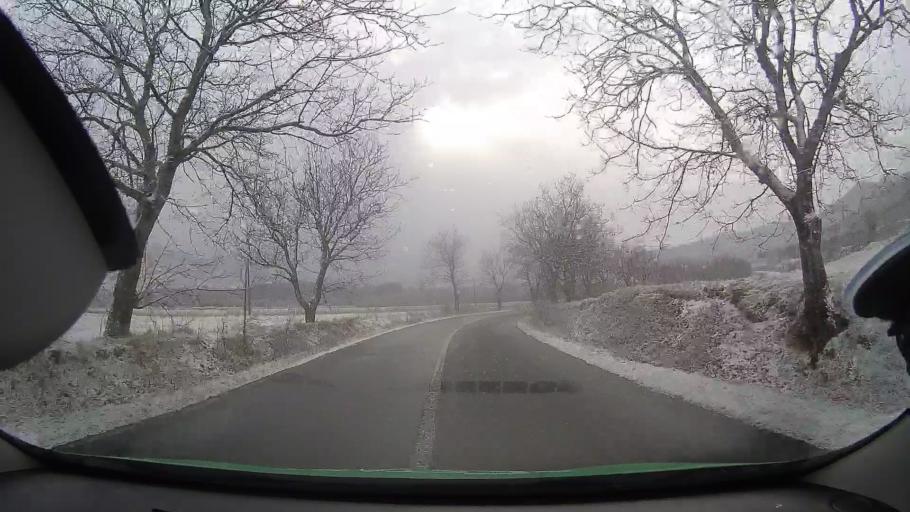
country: RO
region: Alba
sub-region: Comuna Rimetea
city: Rimetea
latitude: 46.4410
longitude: 23.5638
